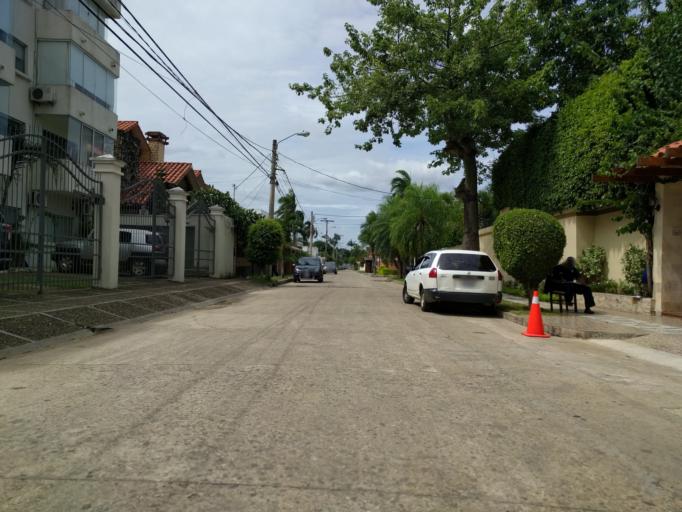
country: BO
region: Santa Cruz
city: Santa Cruz de la Sierra
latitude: -17.8059
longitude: -63.2113
